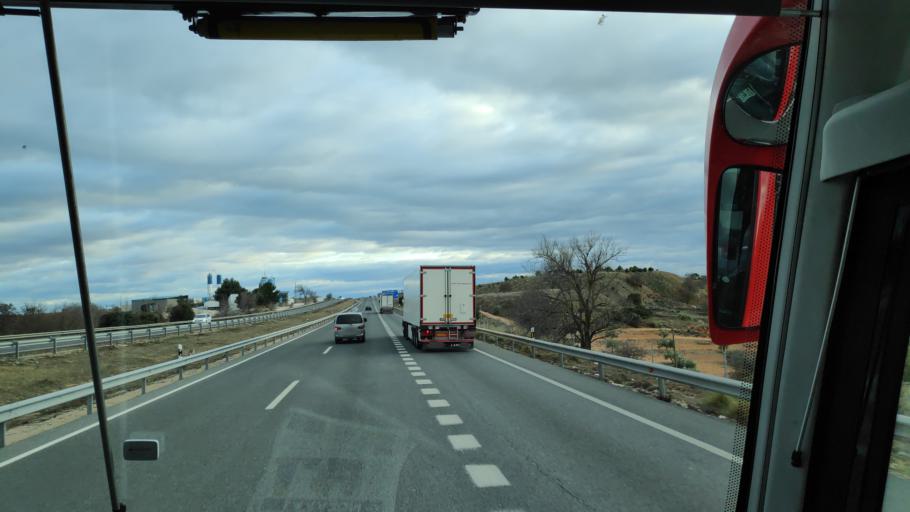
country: ES
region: Madrid
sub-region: Provincia de Madrid
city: Villarejo de Salvanes
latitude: 40.1871
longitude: -3.2985
